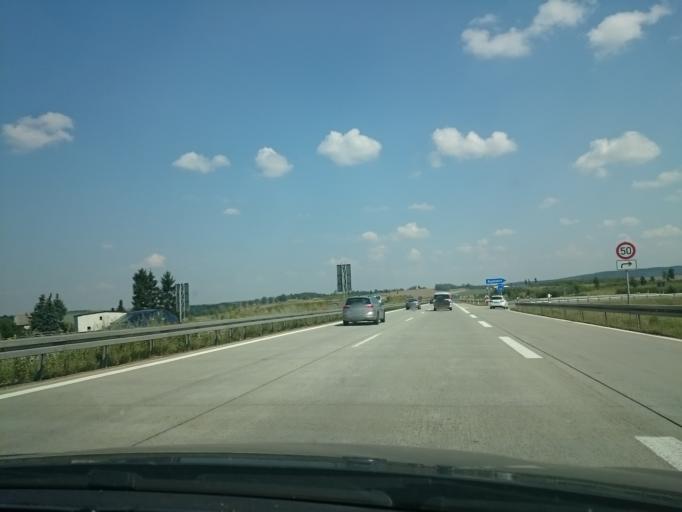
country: DE
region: Saxony
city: Reinsdorf
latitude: 50.6802
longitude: 12.5799
